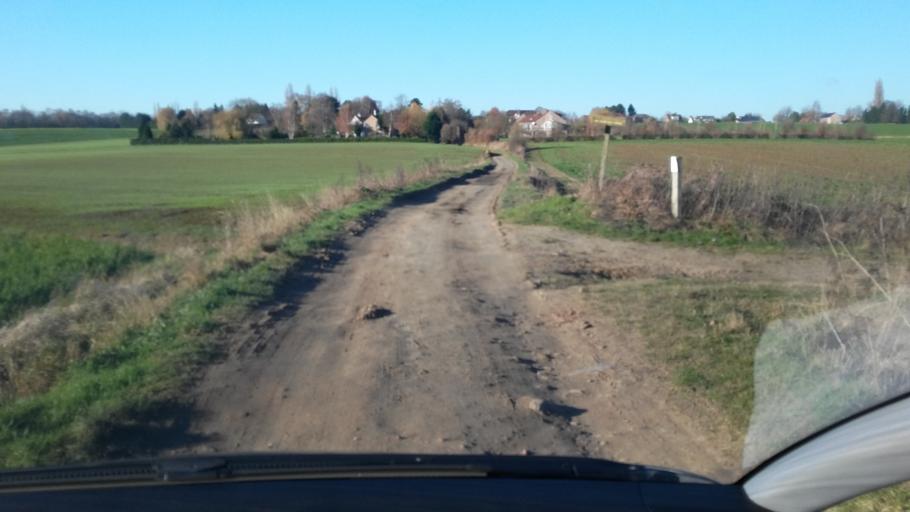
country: BE
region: Wallonia
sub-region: Province du Brabant Wallon
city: Waterloo
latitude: 50.6896
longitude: 4.4235
